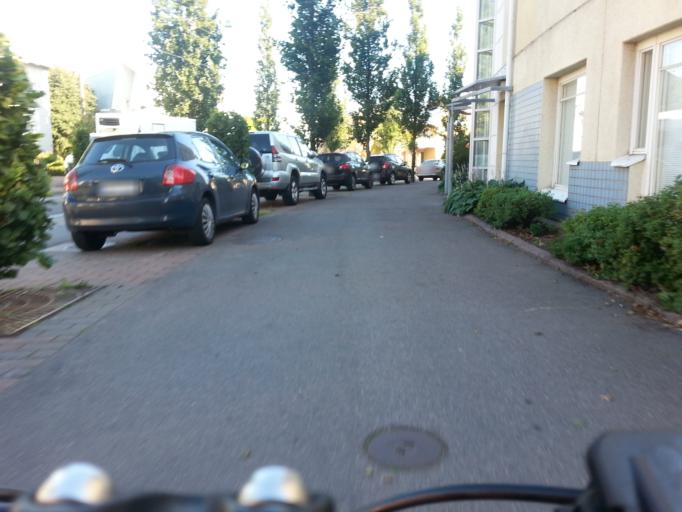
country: FI
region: Uusimaa
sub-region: Helsinki
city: Helsinki
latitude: 60.2065
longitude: 24.8914
